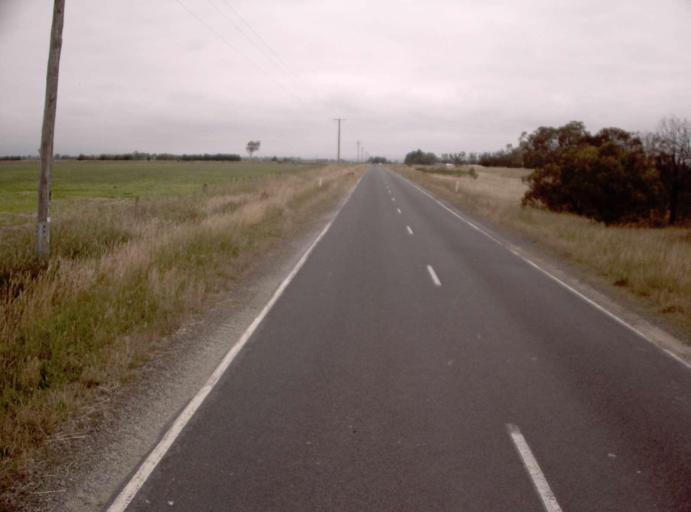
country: AU
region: Victoria
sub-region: Wellington
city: Heyfield
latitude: -38.0346
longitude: 146.7664
